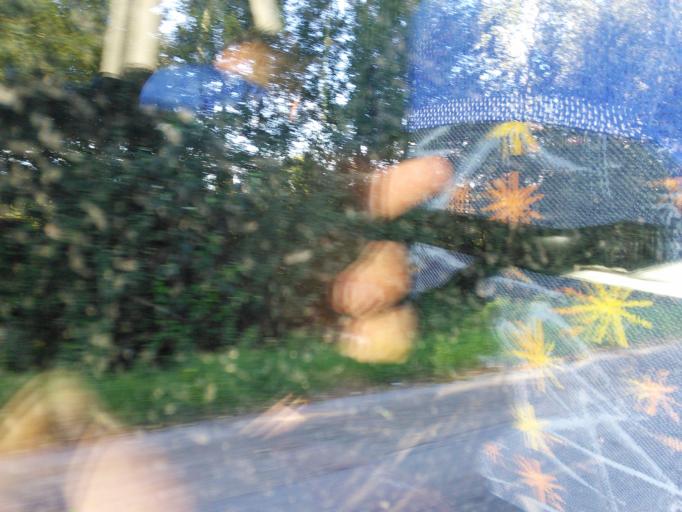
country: RU
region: Jaroslavl
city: Poshekhon'ye
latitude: 58.4956
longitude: 39.0965
